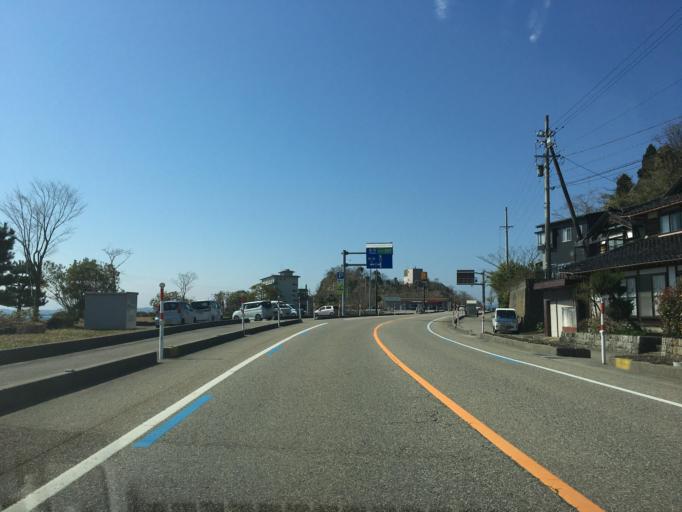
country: JP
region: Toyama
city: Himi
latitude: 36.8883
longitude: 136.9984
